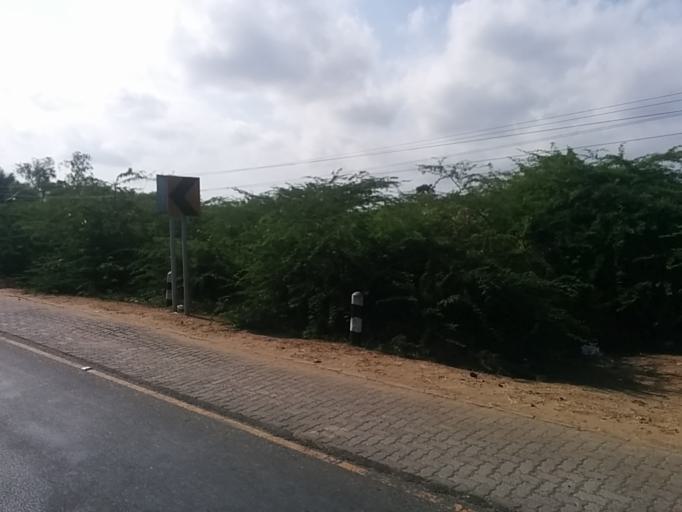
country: IN
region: Tamil Nadu
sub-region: Kancheepuram
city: Mamallapuram
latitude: 12.6179
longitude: 80.1769
